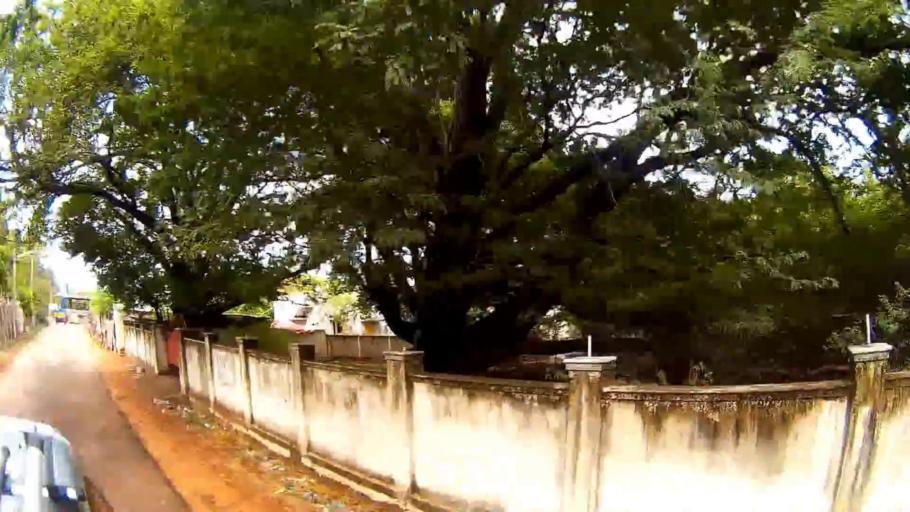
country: VN
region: Lao Cai
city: Sa Pa
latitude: 22.3343
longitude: 103.8419
